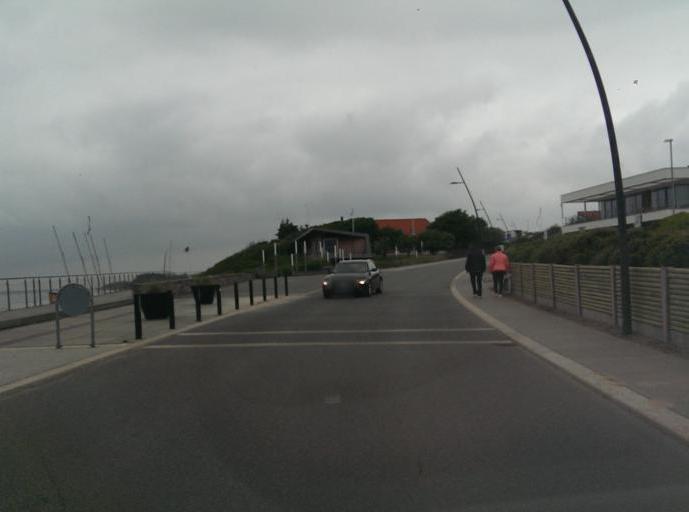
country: DK
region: South Denmark
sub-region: Fano Kommune
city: Nordby
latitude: 55.5271
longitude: 8.3487
